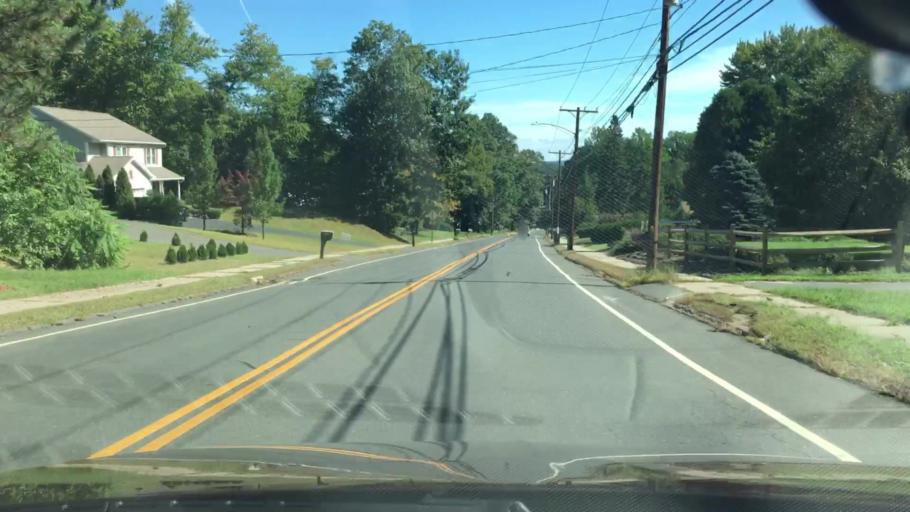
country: US
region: Connecticut
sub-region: Hartford County
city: Bristol
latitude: 41.7031
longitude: -72.9556
